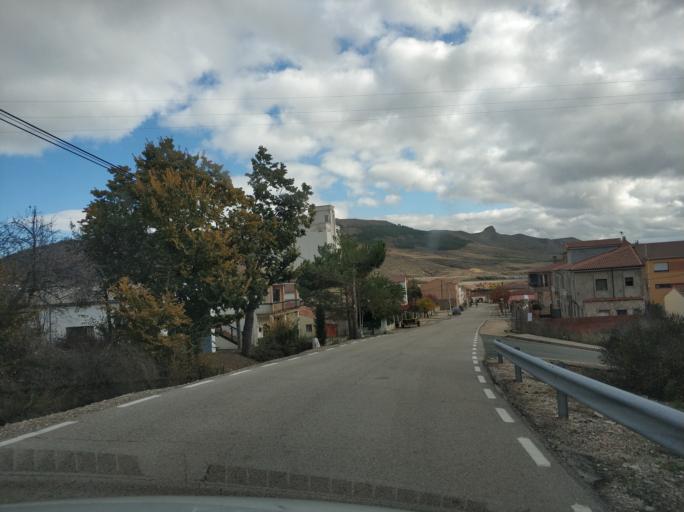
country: ES
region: Castille and Leon
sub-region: Provincia de Soria
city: Medinaceli
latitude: 41.1666
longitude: -2.4249
